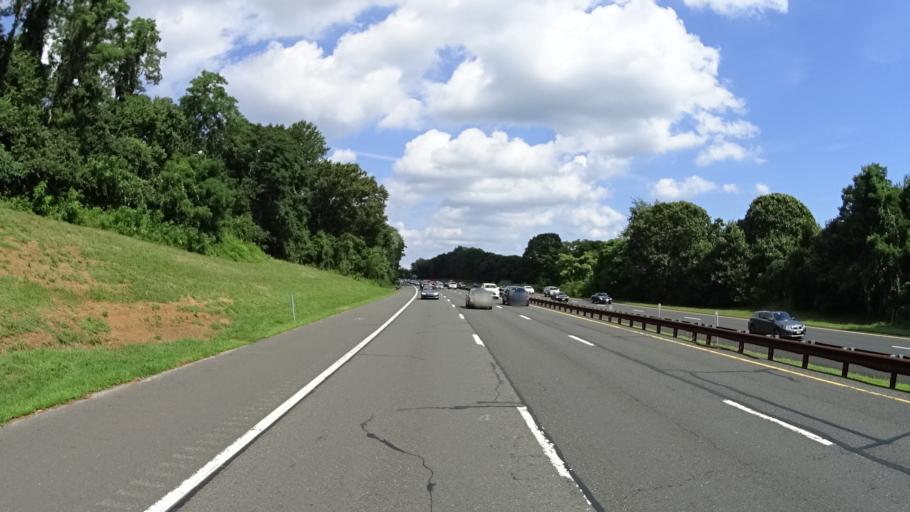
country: US
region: New Jersey
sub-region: Monmouth County
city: Lincroft
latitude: 40.3291
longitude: -74.0988
